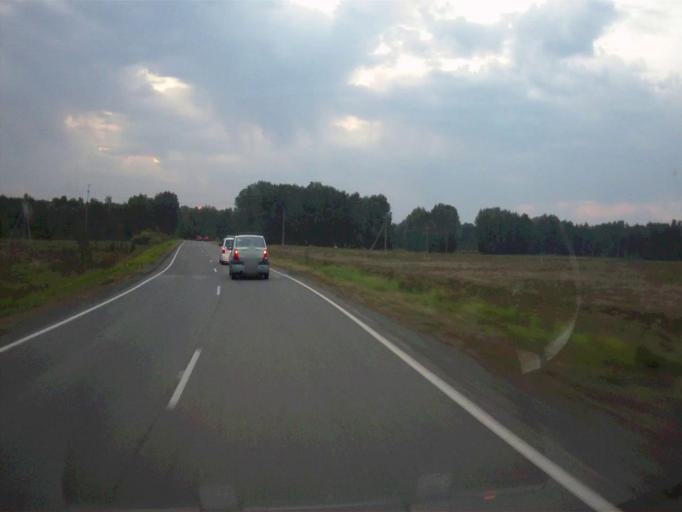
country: RU
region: Chelyabinsk
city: Chebarkul'
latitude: 55.1828
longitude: 60.4731
